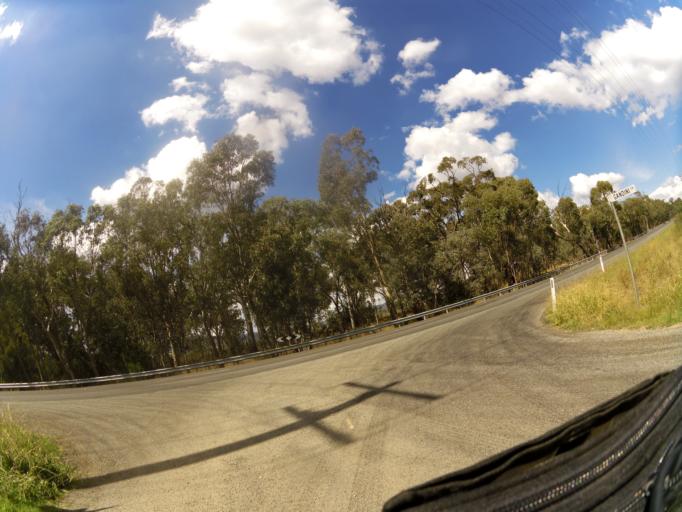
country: AU
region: Victoria
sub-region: Benalla
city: Benalla
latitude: -36.7840
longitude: 146.0099
